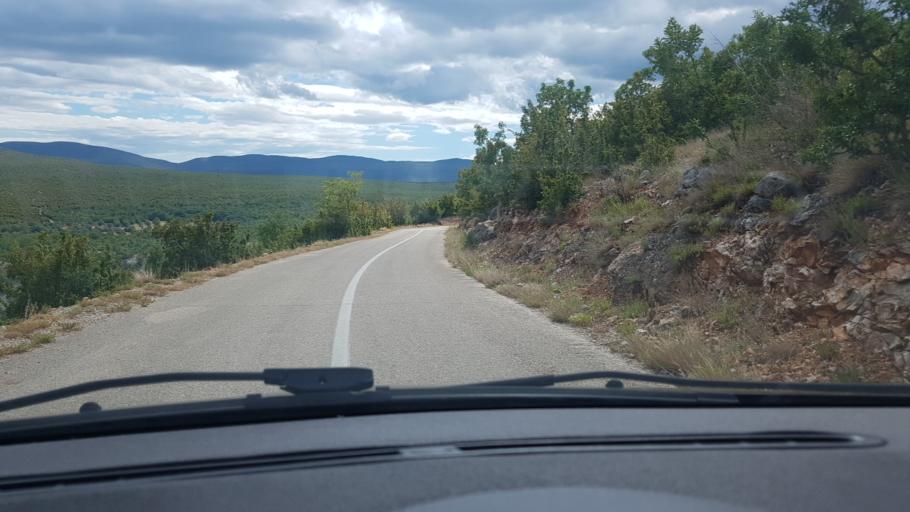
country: HR
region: Zadarska
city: Gracac
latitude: 44.1953
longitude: 15.8773
